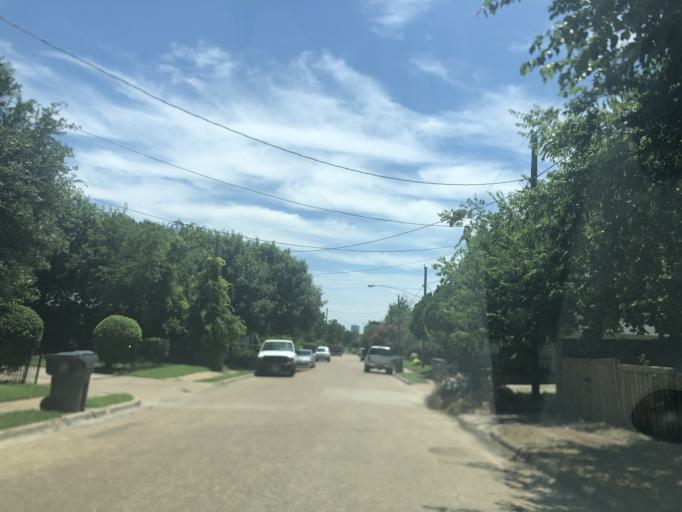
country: US
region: Texas
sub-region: Dallas County
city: Dallas
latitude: 32.7834
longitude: -96.8528
